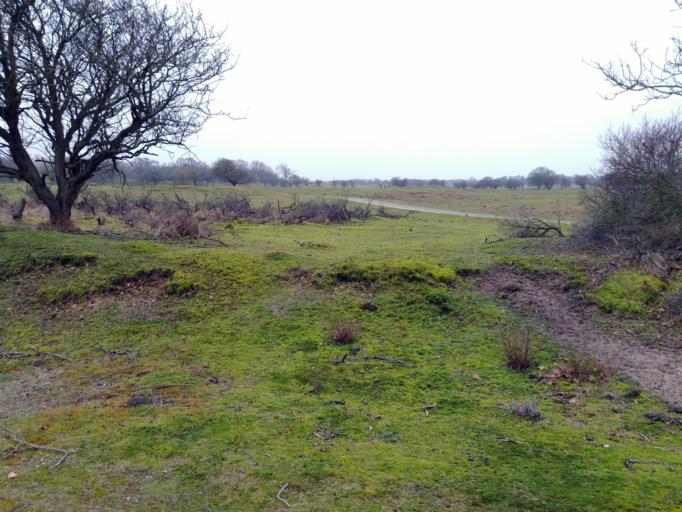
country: NL
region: South Holland
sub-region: Gemeente Hillegom
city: Hillegom
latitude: 52.3201
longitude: 4.5434
